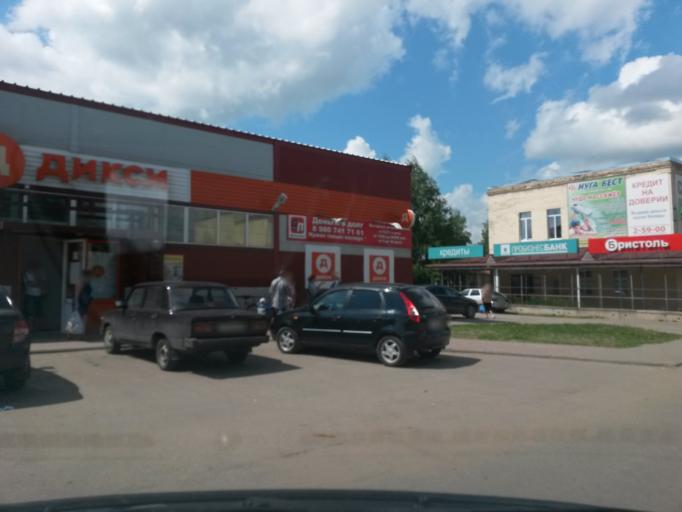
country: RU
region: Jaroslavl
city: Gavrilov-Yam
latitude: 57.3062
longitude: 39.8577
